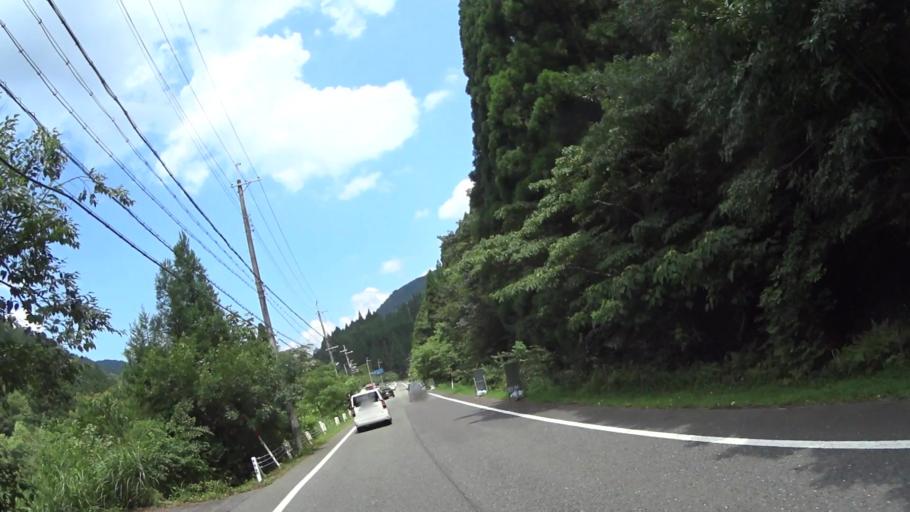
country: JP
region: Shiga Prefecture
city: Kitahama
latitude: 35.3001
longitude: 135.8863
